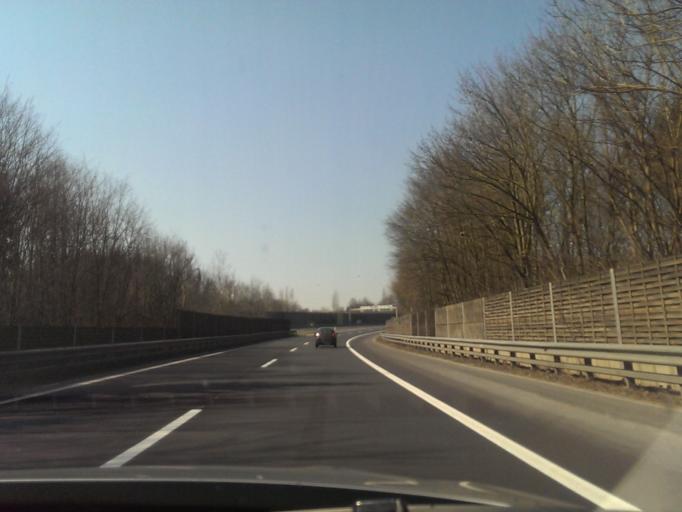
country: AT
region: Upper Austria
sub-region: Wels Stadt
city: Wels
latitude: 48.1801
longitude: 13.9850
